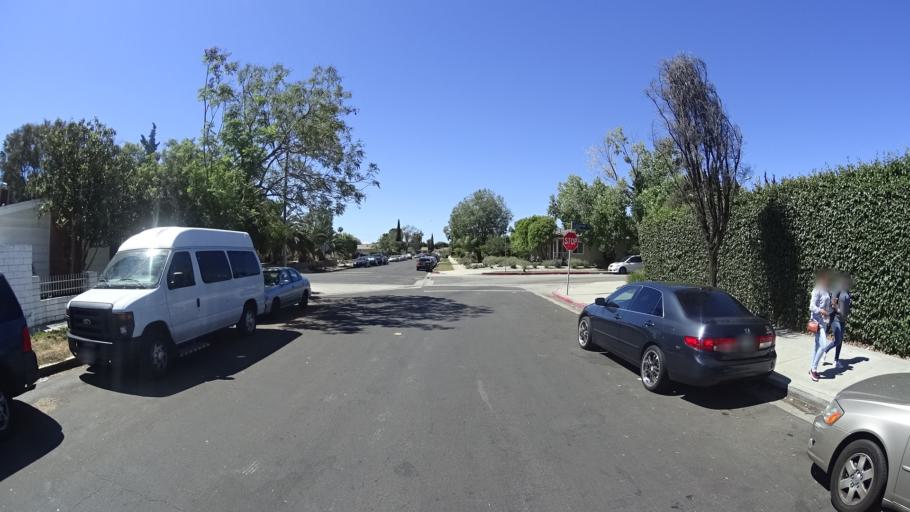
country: US
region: California
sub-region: Los Angeles County
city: San Fernando
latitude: 34.2557
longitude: -118.4660
